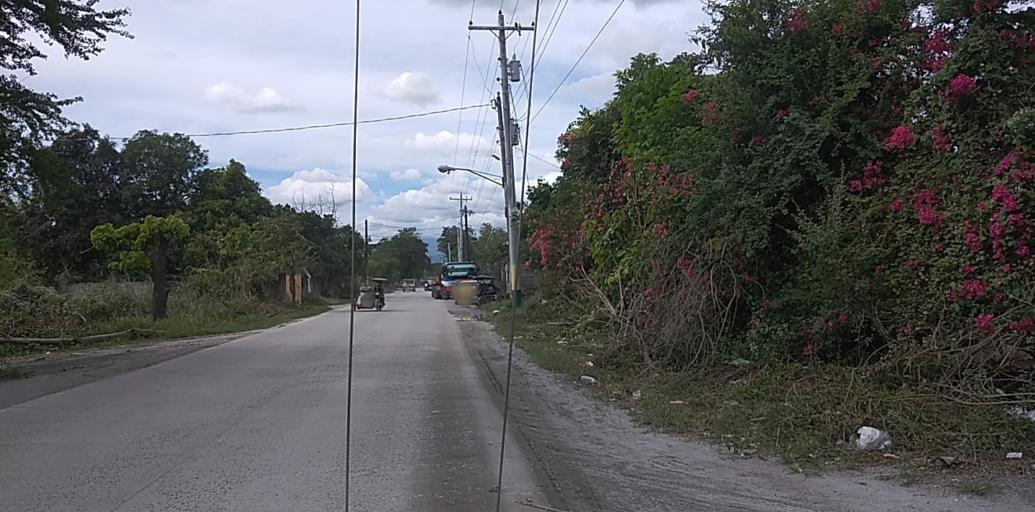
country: PH
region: Central Luzon
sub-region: Province of Pampanga
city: Balas
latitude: 15.0662
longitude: 120.5713
